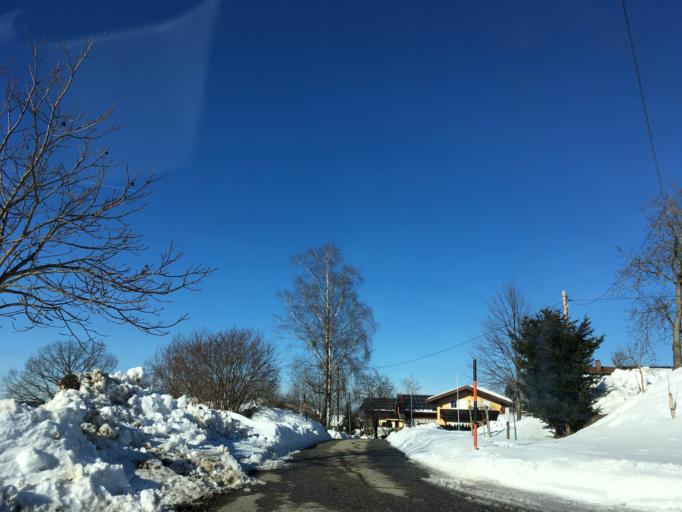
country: DE
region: Bavaria
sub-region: Upper Bavaria
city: Frasdorf
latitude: 47.8039
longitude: 12.3074
